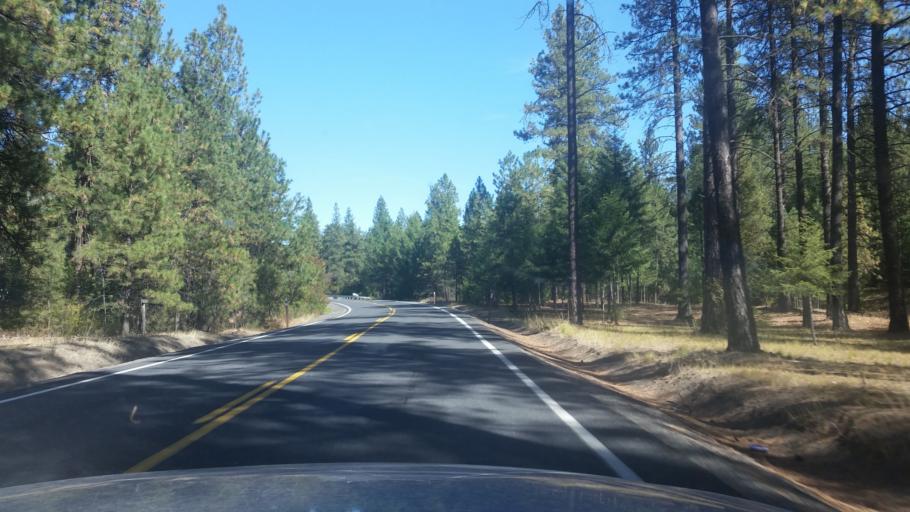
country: US
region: Washington
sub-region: Spokane County
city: Spokane
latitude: 47.5714
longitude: -117.4752
